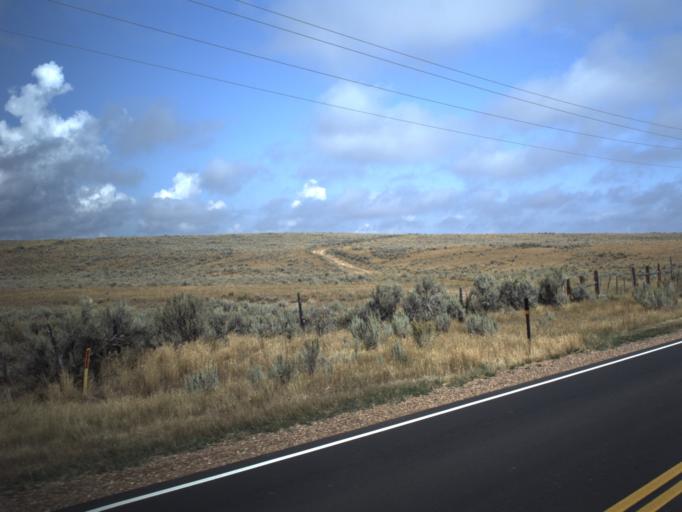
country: US
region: Utah
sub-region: Rich County
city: Randolph
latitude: 41.7347
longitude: -111.1582
